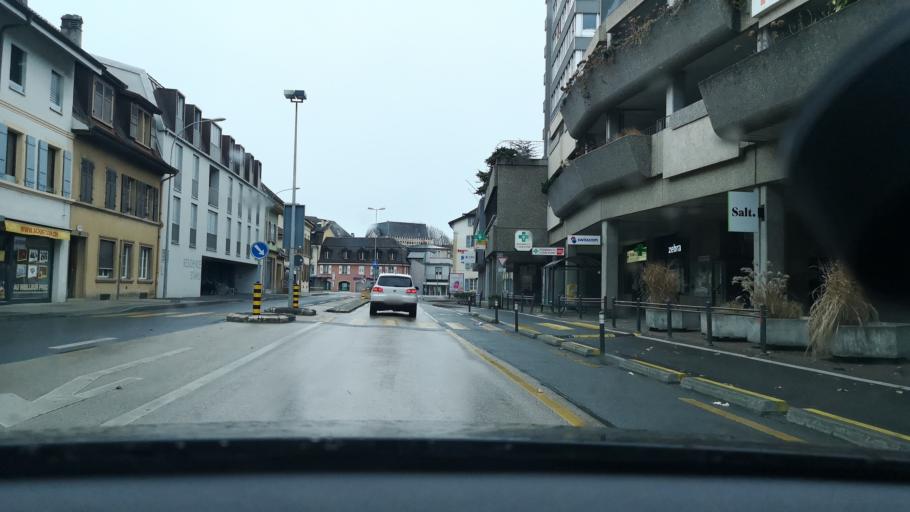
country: CH
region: Vaud
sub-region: Jura-Nord vaudois District
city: Yverdon-les-Bains
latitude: 46.7814
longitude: 6.6362
